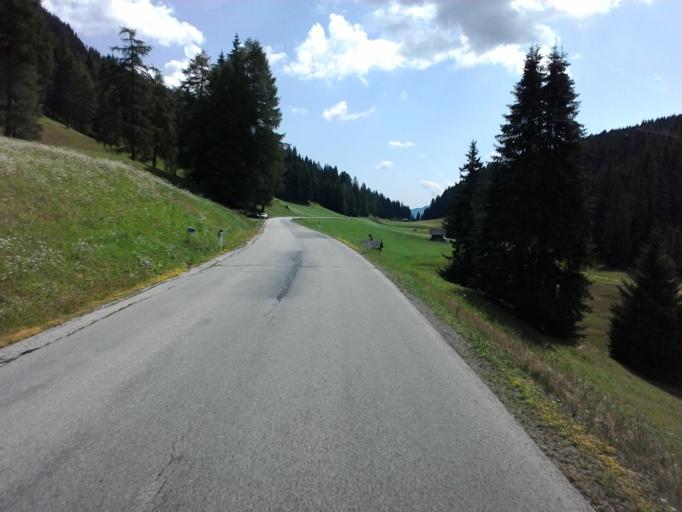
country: AT
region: Tyrol
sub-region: Politischer Bezirk Lienz
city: Kartitsch
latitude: 46.7189
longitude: 12.5319
